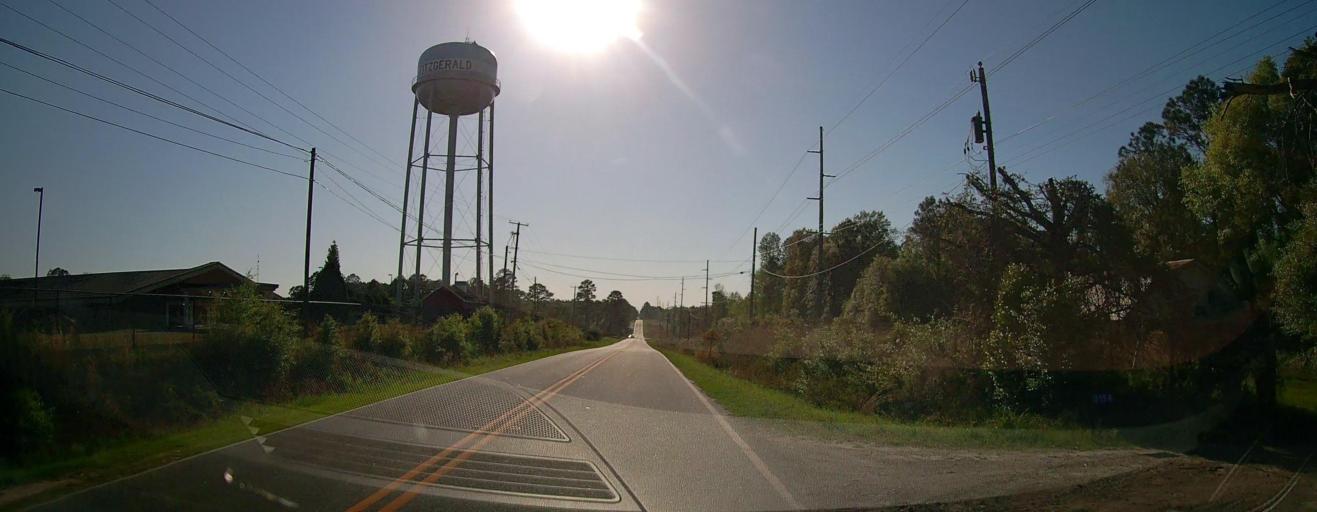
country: US
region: Georgia
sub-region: Ben Hill County
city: Fitzgerald
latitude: 31.7436
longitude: -83.2571
